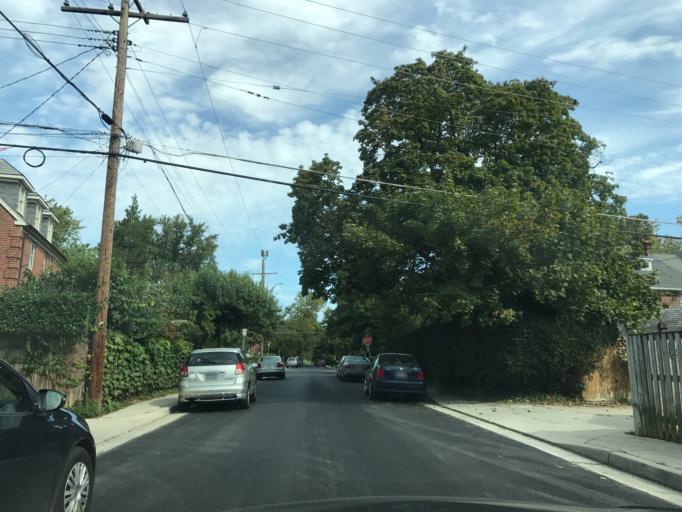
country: US
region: Maryland
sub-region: Baltimore County
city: Towson
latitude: 39.3768
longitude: -76.6142
